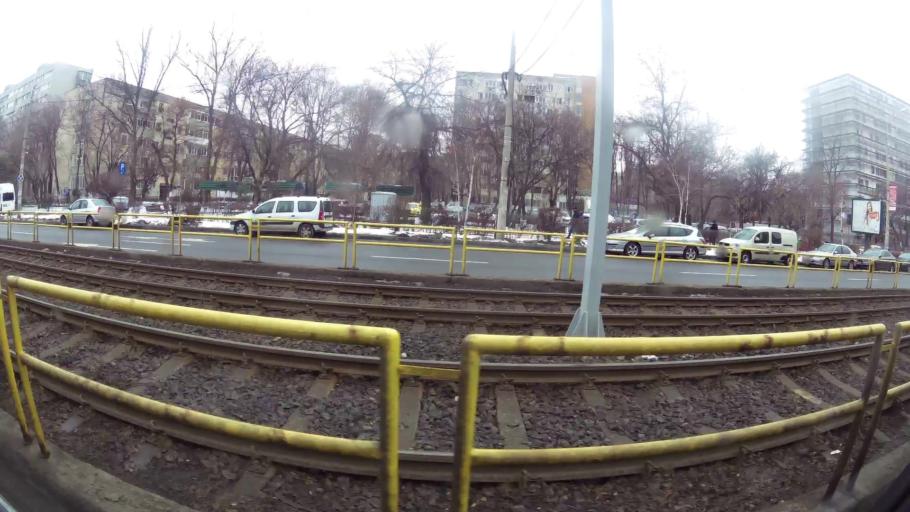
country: RO
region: Ilfov
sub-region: Comuna Chiajna
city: Rosu
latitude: 44.4255
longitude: 26.0338
